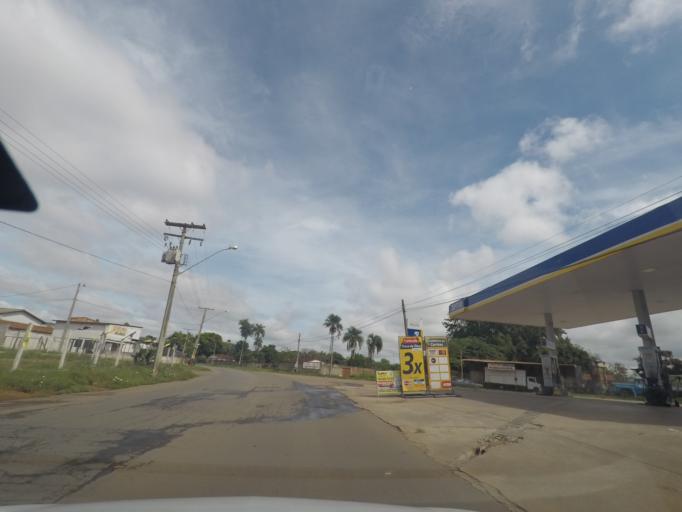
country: BR
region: Goias
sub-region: Goiania
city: Goiania
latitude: -16.6735
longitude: -49.2017
